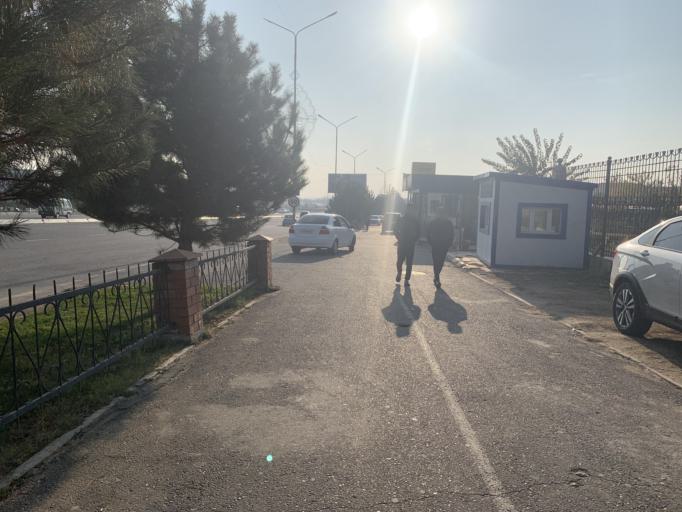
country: UZ
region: Namangan
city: Namangan Shahri
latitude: 40.9981
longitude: 71.5972
